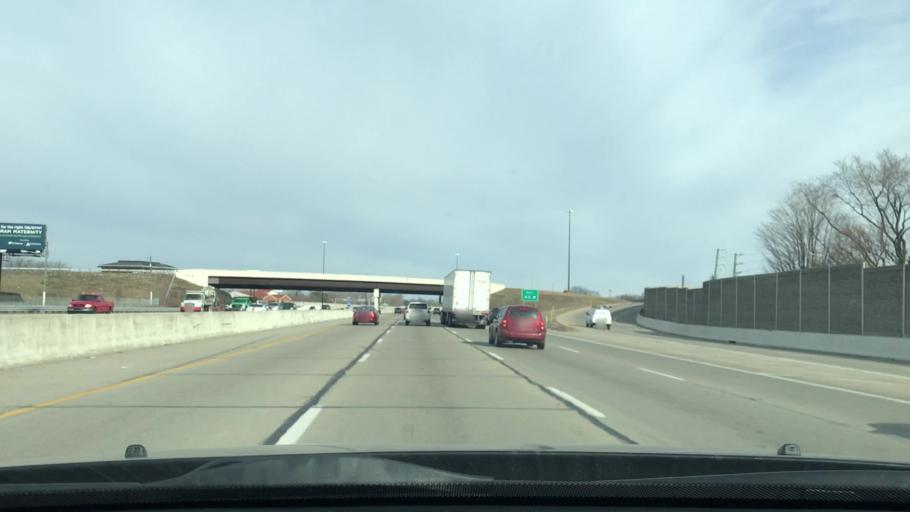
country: US
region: Indiana
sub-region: Marion County
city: Lawrence
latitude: 39.8449
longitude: -86.0428
